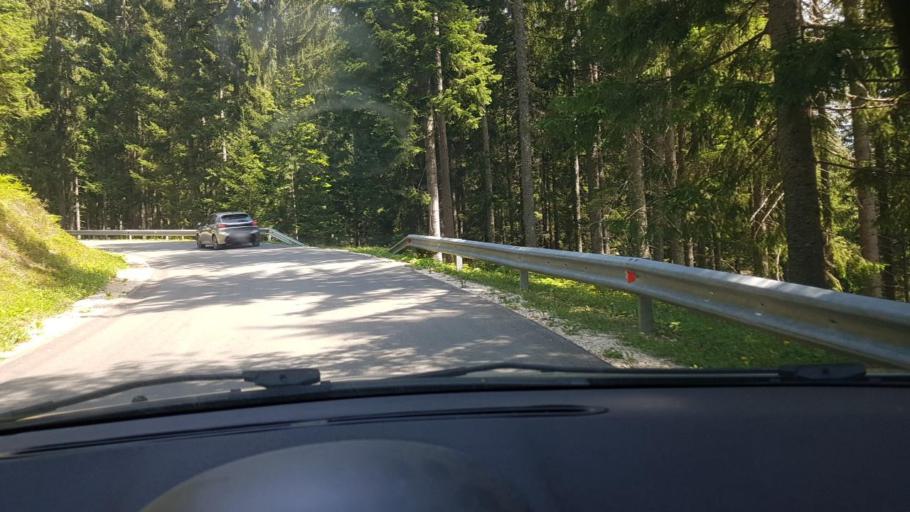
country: AT
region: Carinthia
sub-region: Politischer Bezirk Volkermarkt
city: Bad Eisenkappel
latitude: 46.4252
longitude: 14.5997
